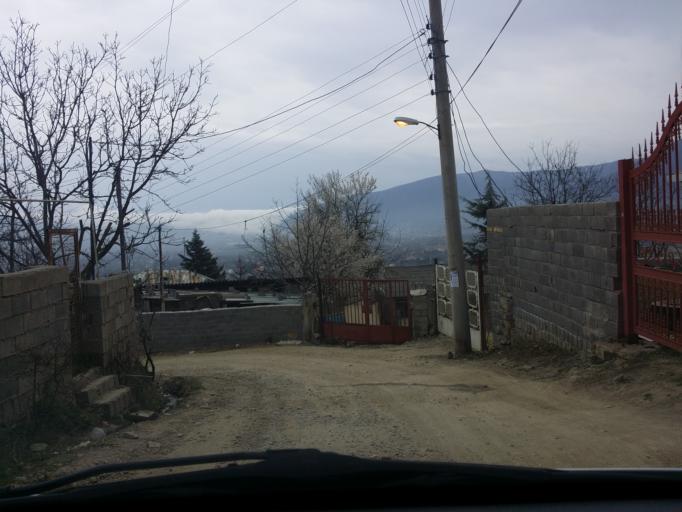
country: IR
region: Mazandaran
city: `Abbasabad
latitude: 36.5322
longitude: 51.1593
